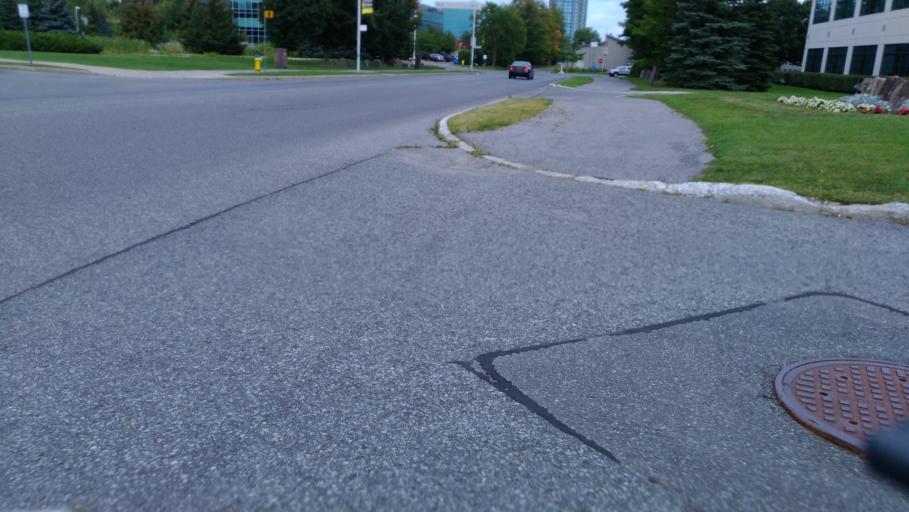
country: CA
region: Ontario
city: Bells Corners
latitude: 45.3436
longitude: -75.9236
